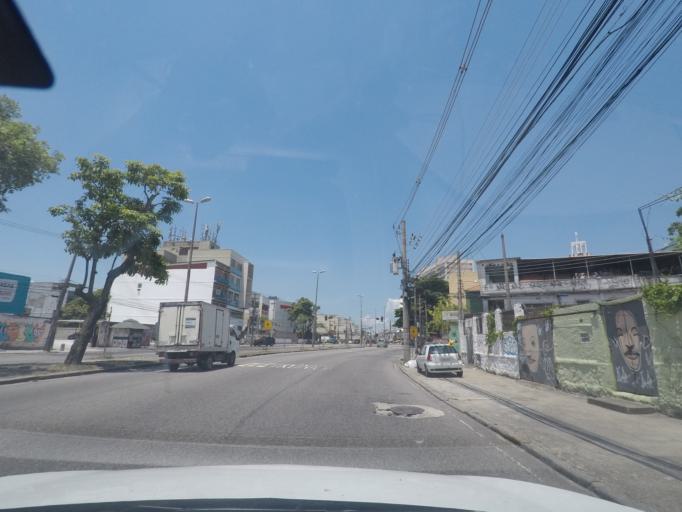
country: BR
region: Rio de Janeiro
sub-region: Rio De Janeiro
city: Rio de Janeiro
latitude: -22.8820
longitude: -43.2947
